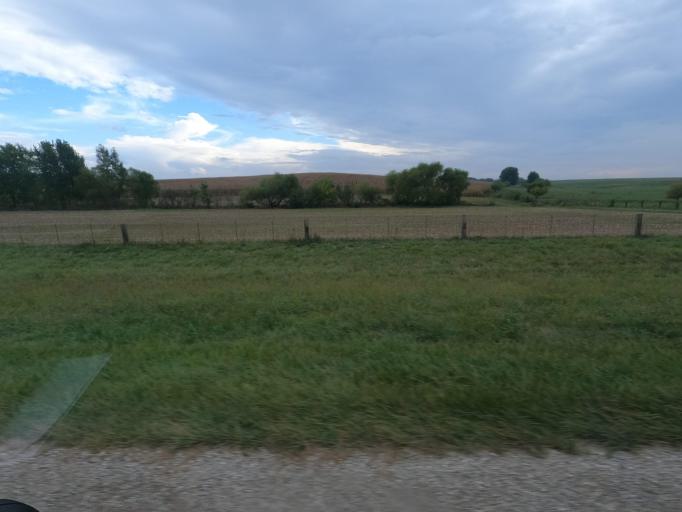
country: US
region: Iowa
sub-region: Henry County
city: Mount Pleasant
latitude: 40.7845
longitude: -91.6890
